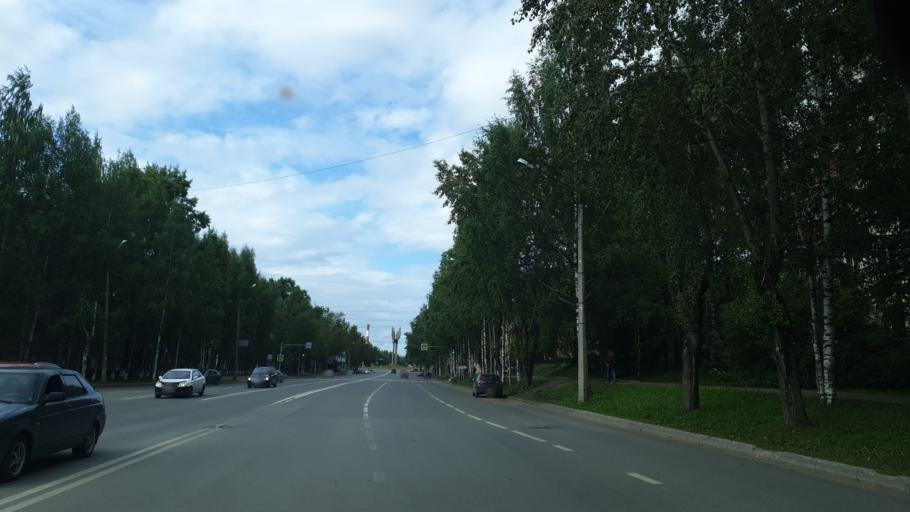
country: RU
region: Komi Republic
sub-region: Syktyvdinskiy Rayon
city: Syktyvkar
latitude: 61.6608
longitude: 50.8193
